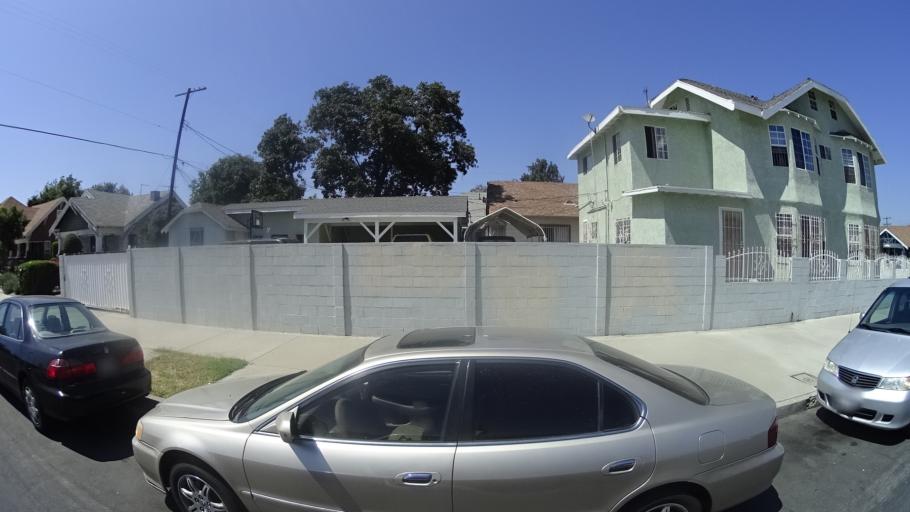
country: US
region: California
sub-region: Los Angeles County
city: View Park-Windsor Hills
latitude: 33.9987
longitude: -118.2963
